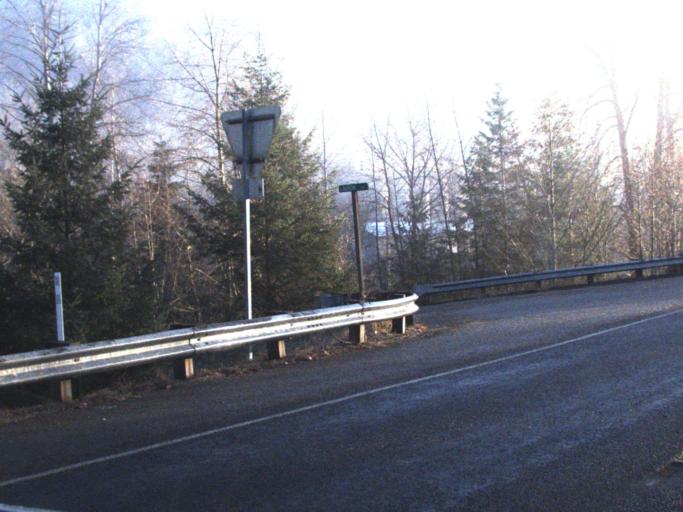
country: US
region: Washington
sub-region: Snohomish County
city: Darrington
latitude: 48.5369
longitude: -121.7436
